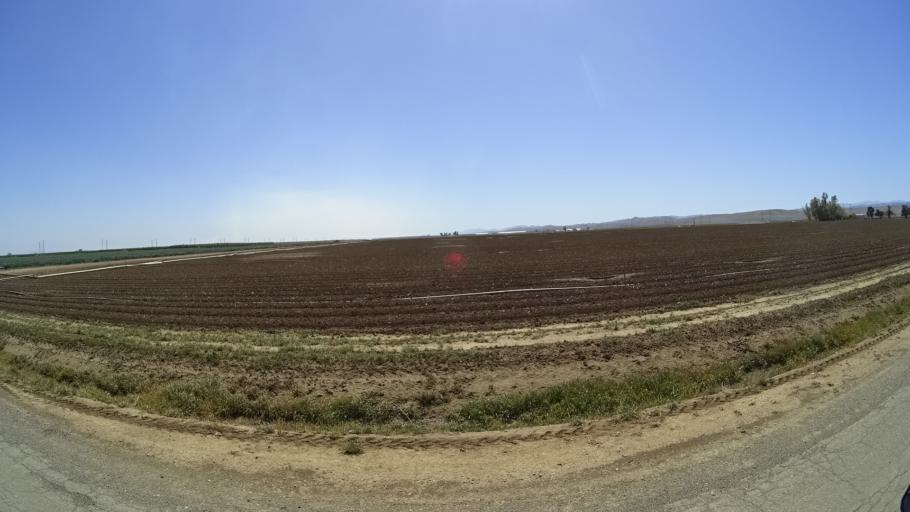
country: US
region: California
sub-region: Glenn County
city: Willows
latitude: 39.4657
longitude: -122.2734
